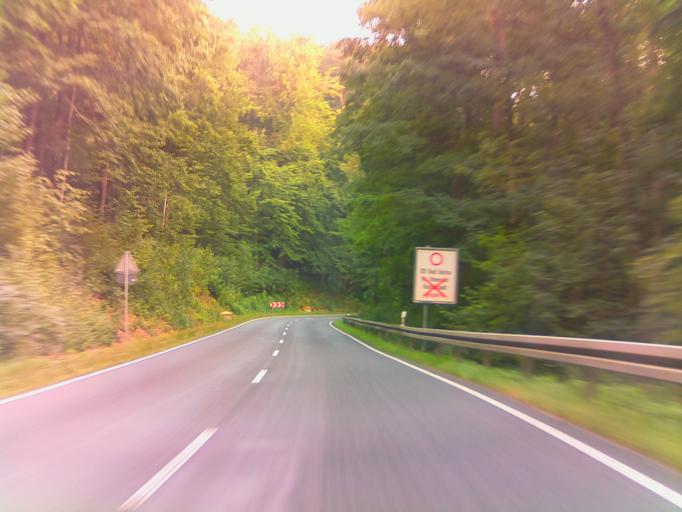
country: DE
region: Thuringia
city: Troistedt
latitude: 50.9209
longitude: 11.2546
